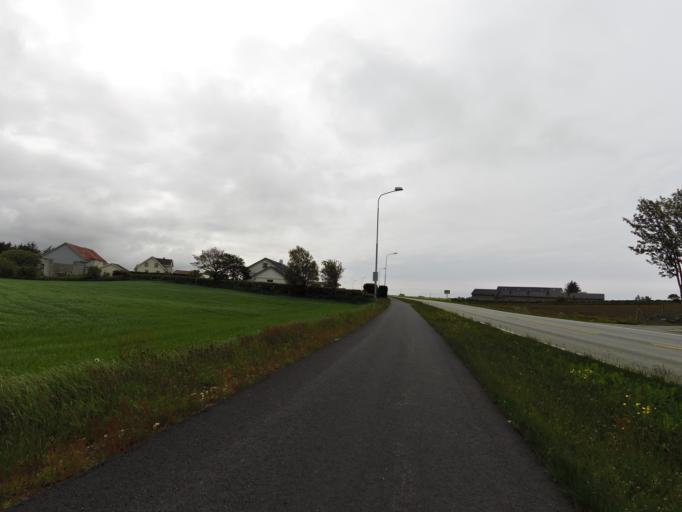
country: NO
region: Rogaland
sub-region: Klepp
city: Kleppe
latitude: 58.8271
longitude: 5.5906
